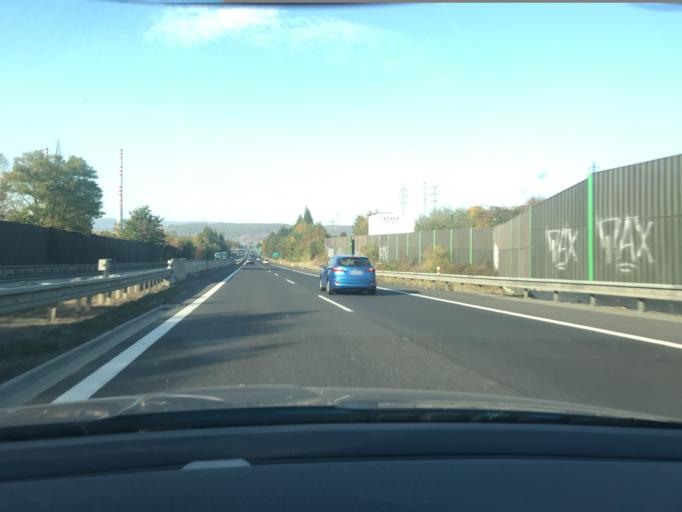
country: CZ
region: Ustecky
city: Trmice
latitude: 50.6323
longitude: 13.9921
